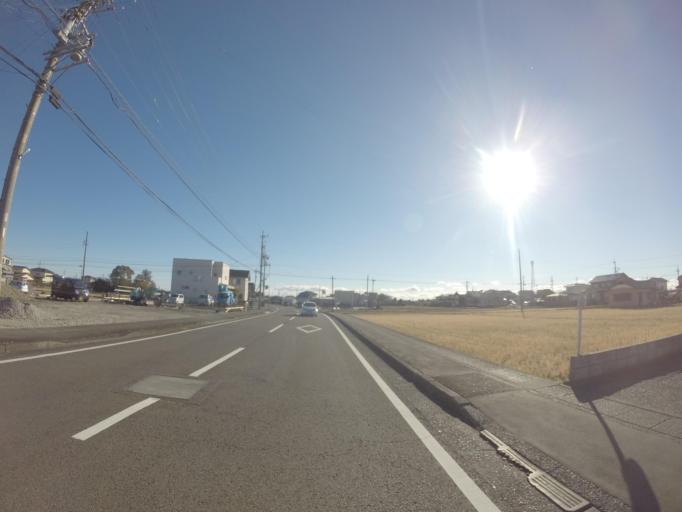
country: JP
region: Shizuoka
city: Fujieda
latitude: 34.8328
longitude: 138.2575
